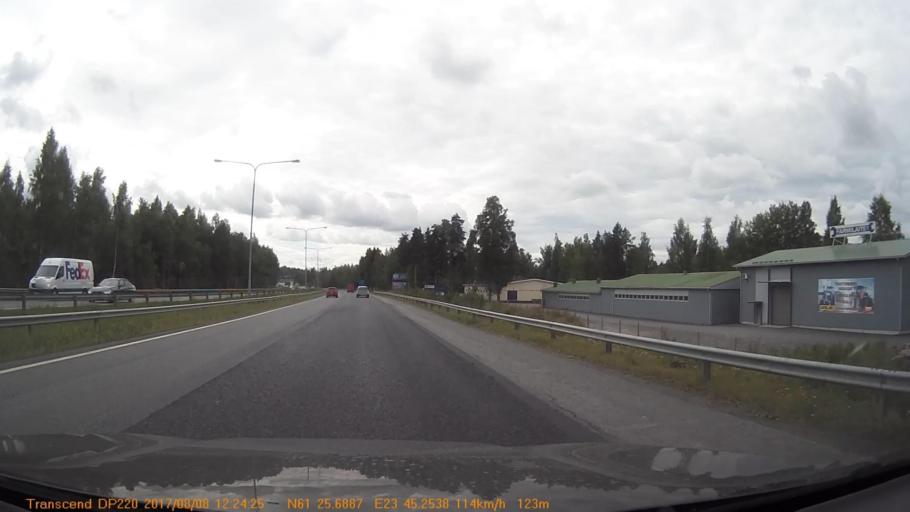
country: FI
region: Pirkanmaa
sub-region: Tampere
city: Tampere
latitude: 61.4280
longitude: 23.7542
